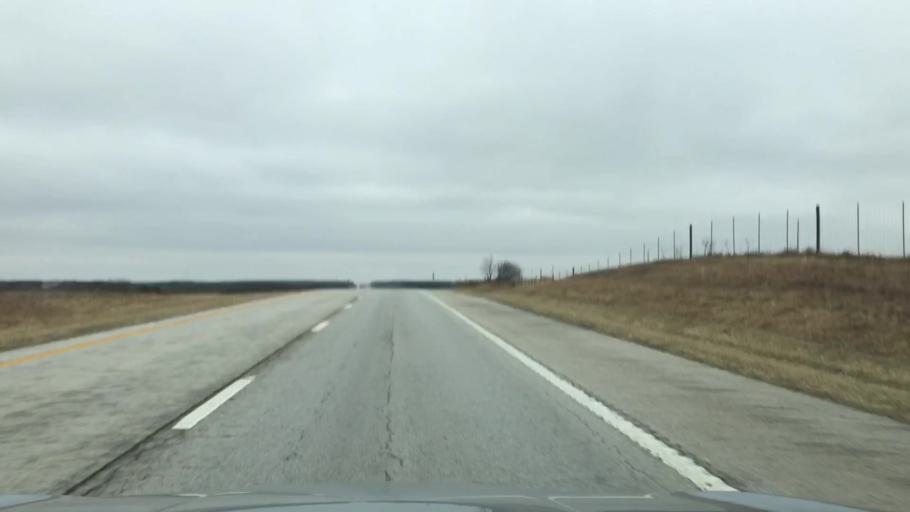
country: US
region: Missouri
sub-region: Linn County
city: Marceline
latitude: 39.7593
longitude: -92.8869
